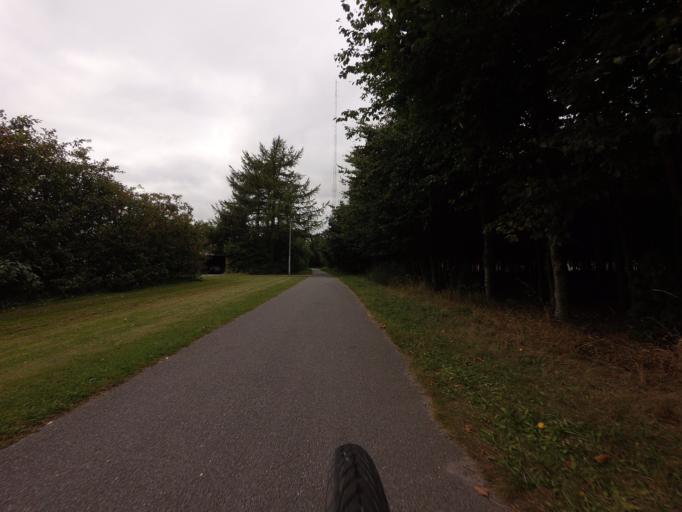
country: DK
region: South Denmark
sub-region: Billund Kommune
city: Grindsted
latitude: 55.7649
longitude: 8.9230
